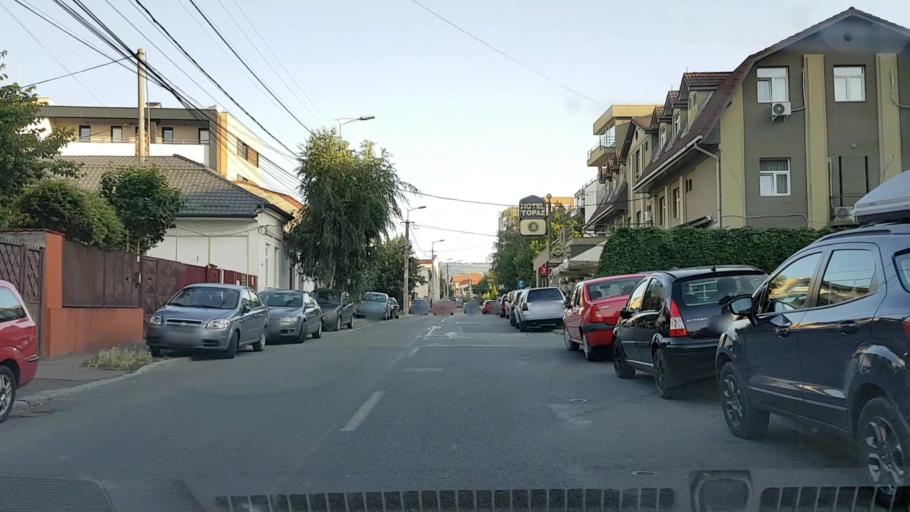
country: RO
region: Cluj
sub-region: Municipiul Cluj-Napoca
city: Cluj-Napoca
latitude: 46.7710
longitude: 23.6091
